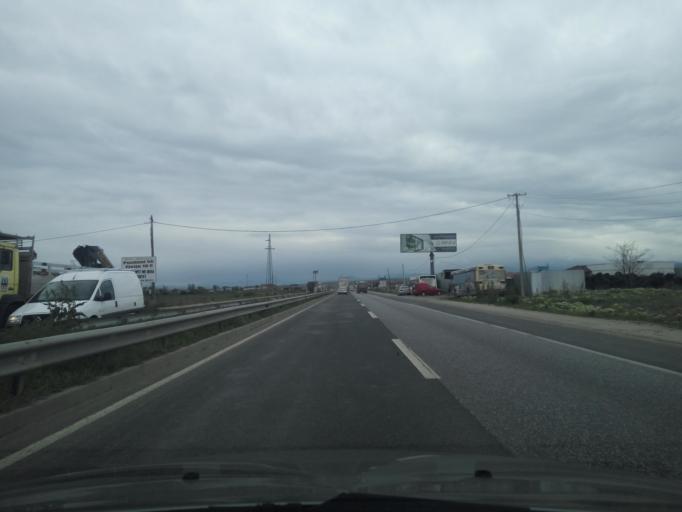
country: XK
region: Pristina
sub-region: Komuna e Obiliqit
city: Obiliq
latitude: 42.7121
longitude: 21.1001
